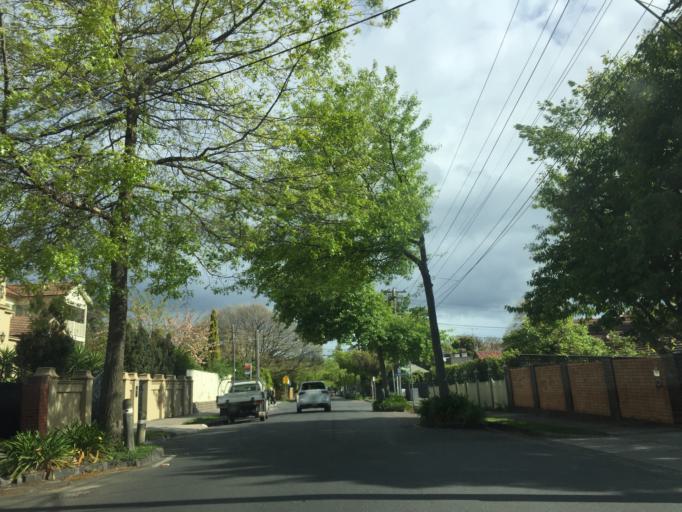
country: AU
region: Victoria
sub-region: Boroondara
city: Kew East
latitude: -37.8051
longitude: 145.0544
